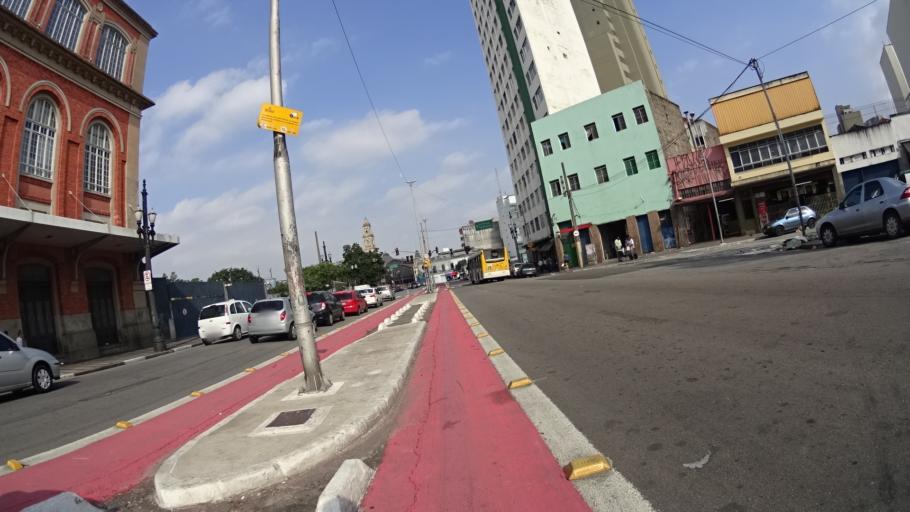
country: BR
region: Sao Paulo
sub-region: Sao Paulo
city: Sao Paulo
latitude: -23.5349
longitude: -46.6387
